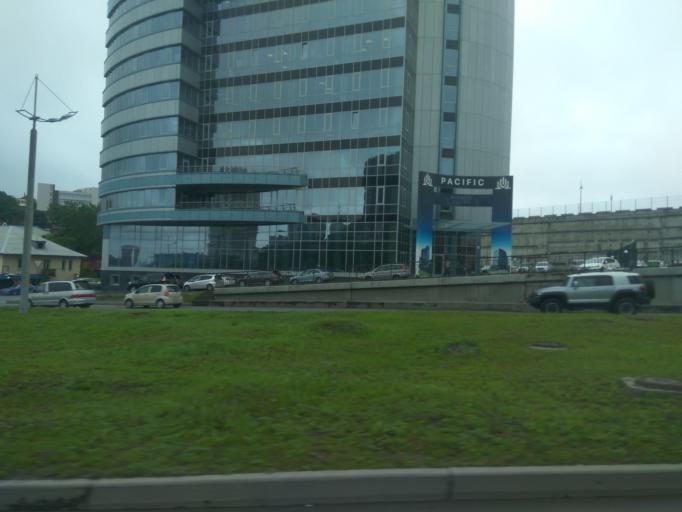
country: RU
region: Primorskiy
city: Vladivostok
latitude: 43.1195
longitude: 131.9021
